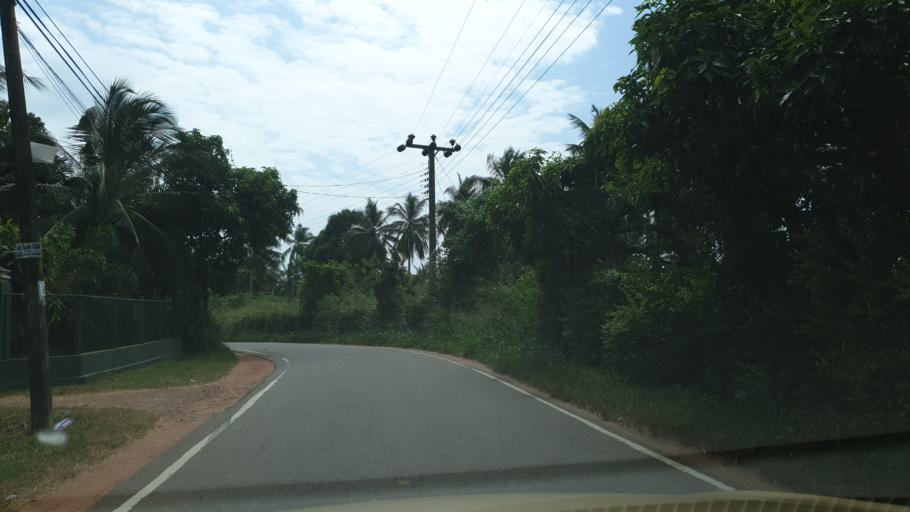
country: LK
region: North Western
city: Kuliyapitiya
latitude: 7.3496
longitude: 79.9786
